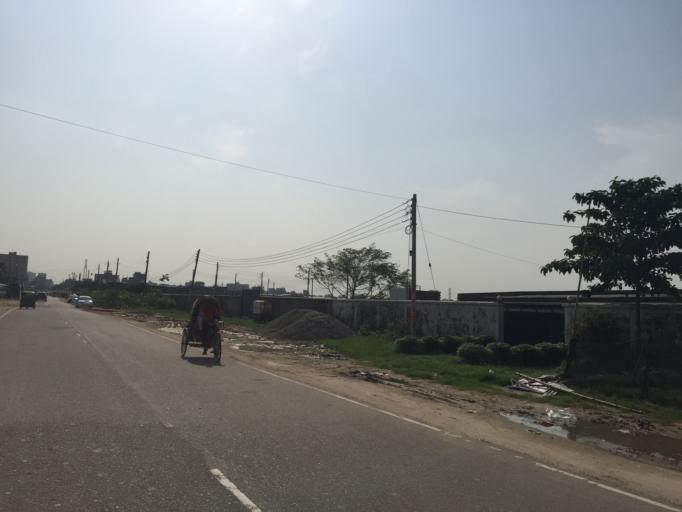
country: BD
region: Dhaka
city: Paltan
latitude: 23.7996
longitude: 90.4431
